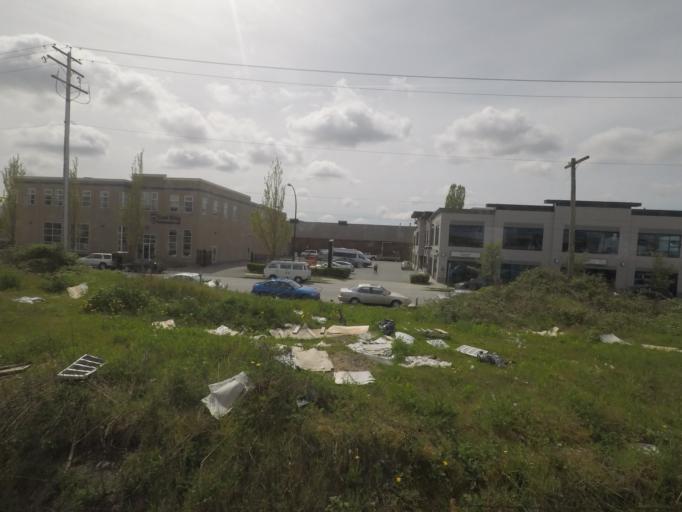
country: CA
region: British Columbia
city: Vancouver
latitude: 49.2724
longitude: -123.0898
